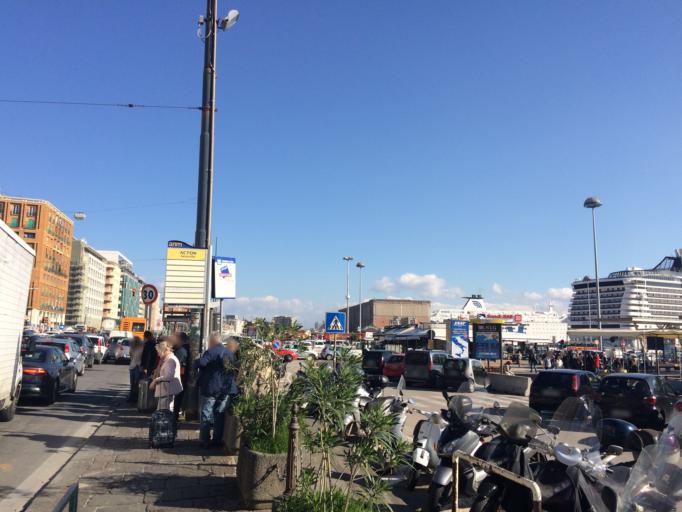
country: IT
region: Campania
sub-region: Provincia di Napoli
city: Napoli
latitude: 40.8380
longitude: 14.2545
